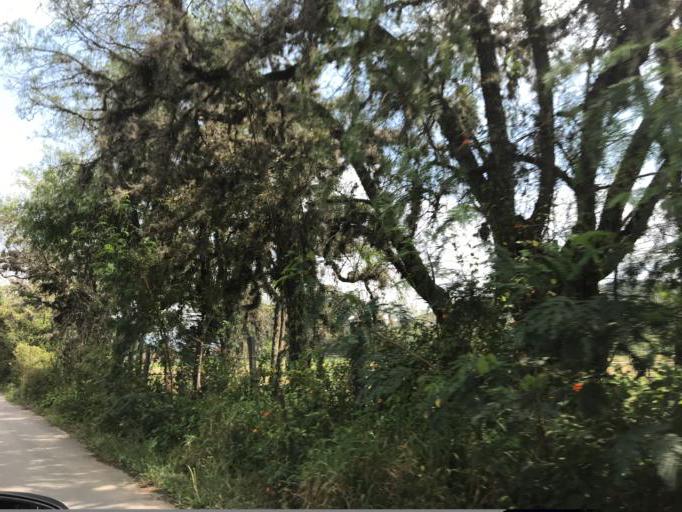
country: CO
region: Boyaca
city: Villa de Leiva
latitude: 5.6554
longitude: -73.5790
